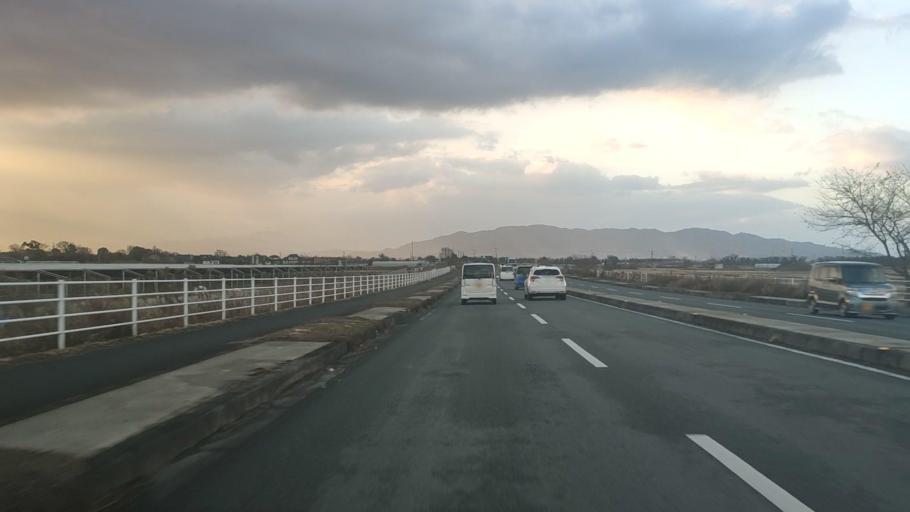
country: JP
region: Kumamoto
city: Kumamoto
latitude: 32.7522
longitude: 130.7066
